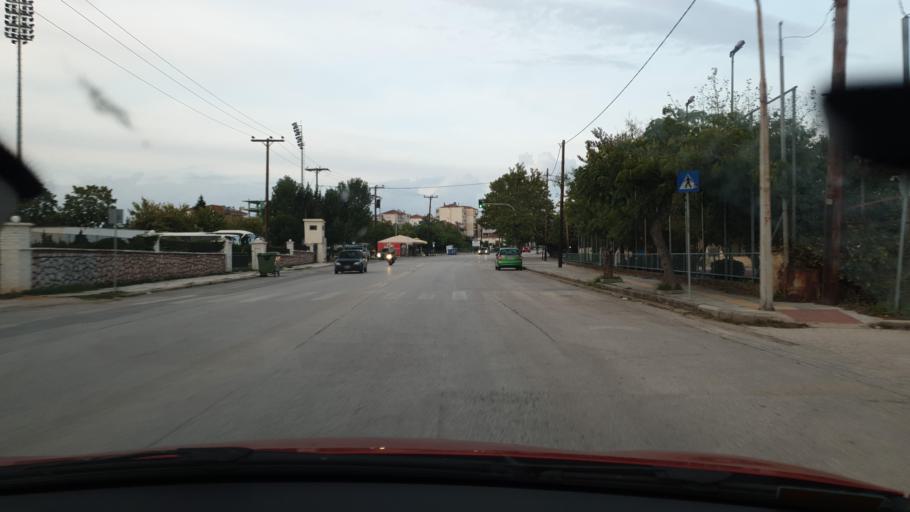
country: GR
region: Central Macedonia
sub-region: Nomos Kilkis
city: Kilkis
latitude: 40.9855
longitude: 22.8653
